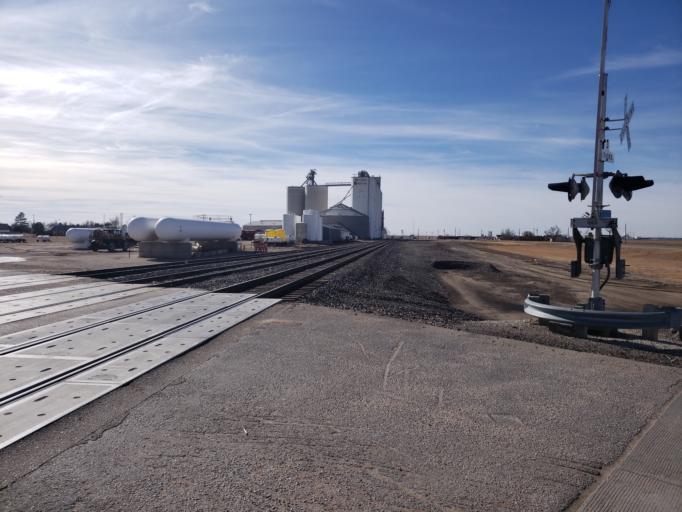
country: US
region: Kansas
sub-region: Ford County
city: Dodge City
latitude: 37.7845
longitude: -99.8875
